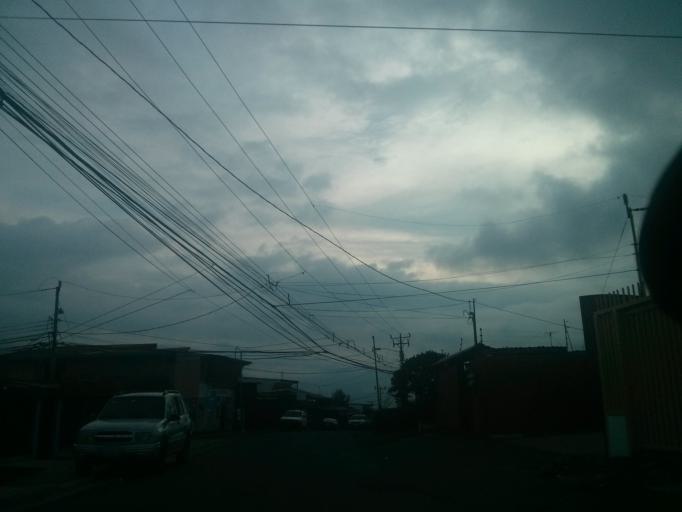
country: CR
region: Heredia
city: San Pablo
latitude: 9.9941
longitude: -84.1045
